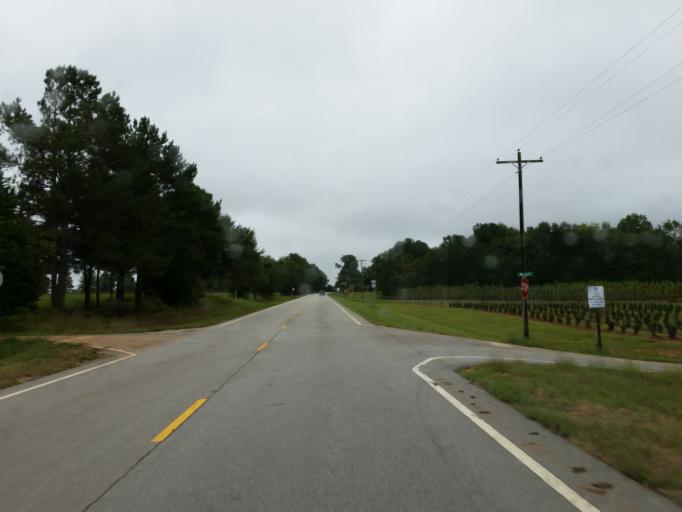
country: US
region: Georgia
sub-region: Lamar County
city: Barnesville
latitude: 32.9729
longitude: -84.1138
